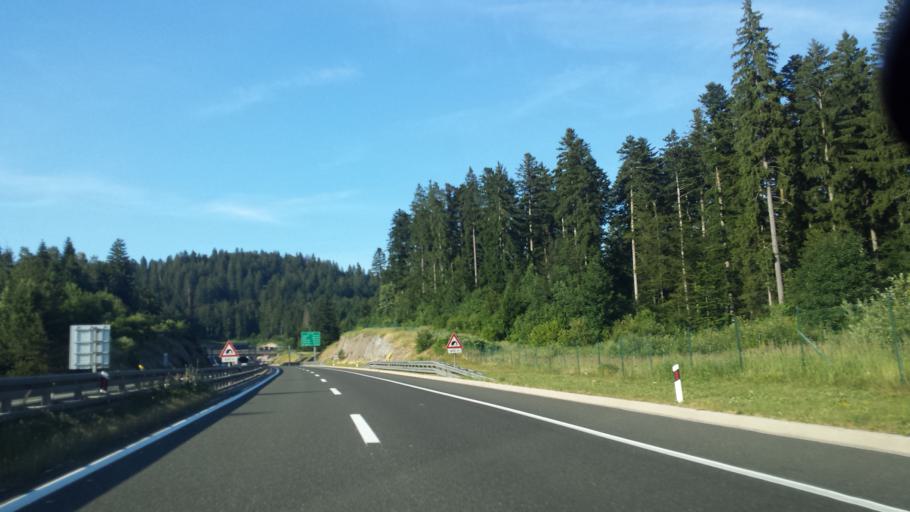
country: HR
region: Primorsko-Goranska
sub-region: Grad Delnice
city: Delnice
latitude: 45.3778
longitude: 14.7973
